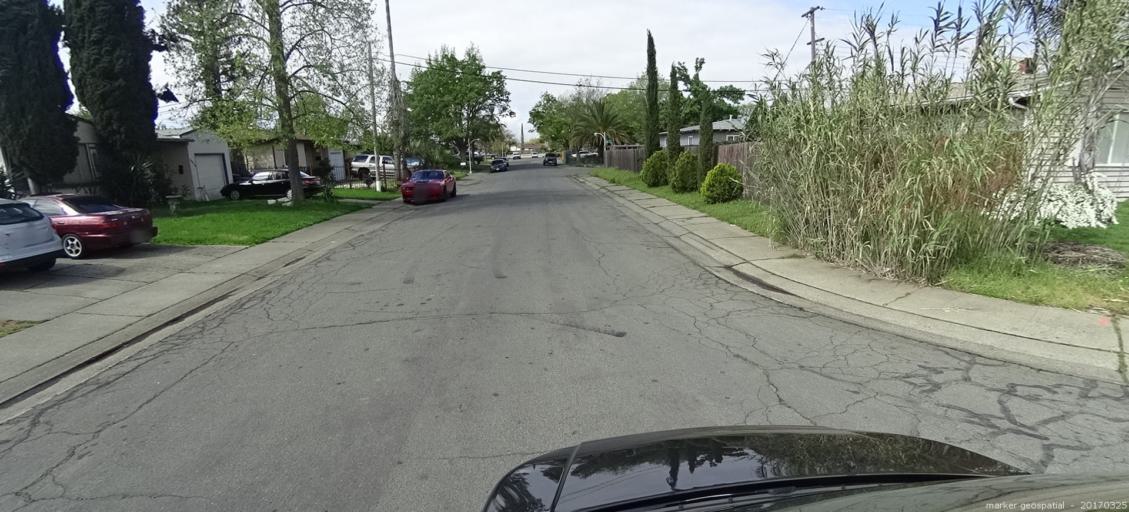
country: US
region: California
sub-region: Sacramento County
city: Florin
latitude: 38.5181
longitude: -121.4249
